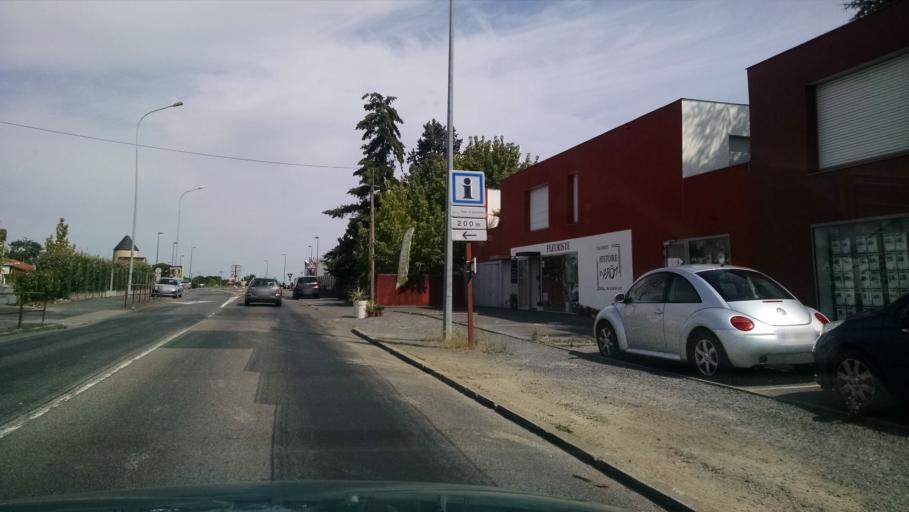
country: FR
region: Pays de la Loire
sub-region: Departement de la Loire-Atlantique
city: Clisson
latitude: 47.0946
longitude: -1.2811
